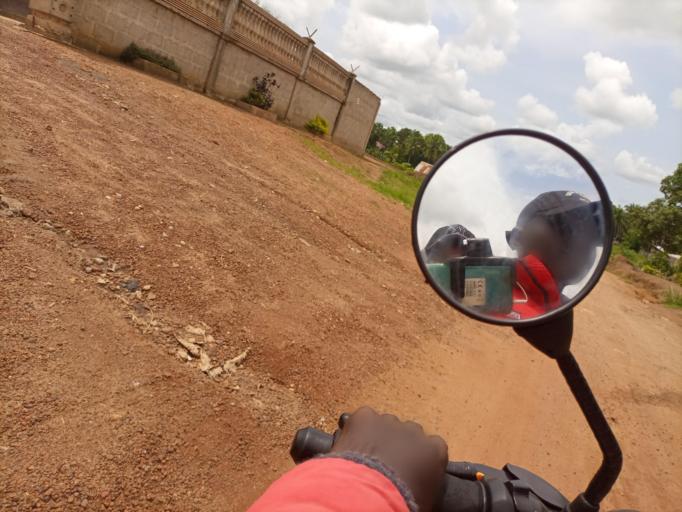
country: SL
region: Southern Province
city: Bo
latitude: 7.9707
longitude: -11.7194
